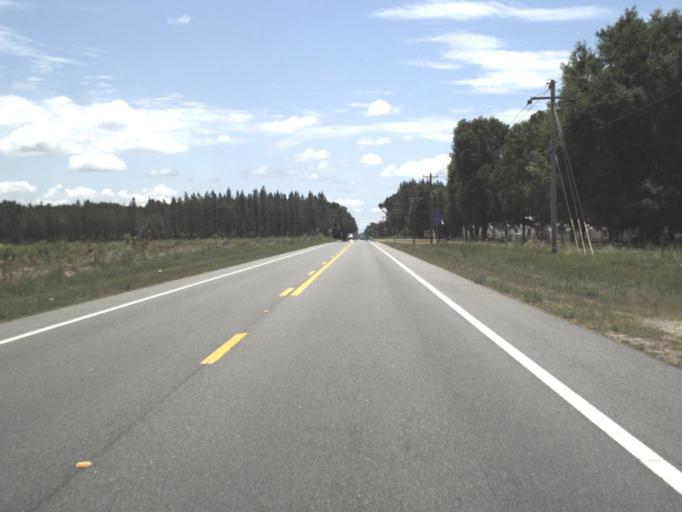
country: US
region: Florida
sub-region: Dixie County
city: Cross City
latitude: 29.7110
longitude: -82.9845
